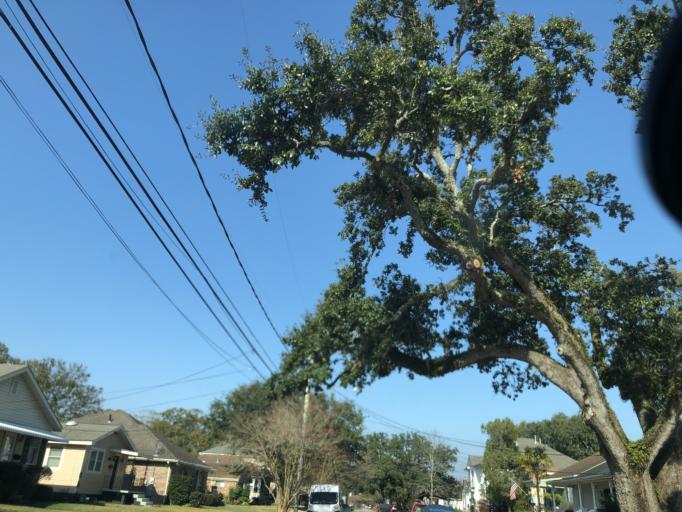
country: US
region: Louisiana
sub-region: Jefferson Parish
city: Metairie
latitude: 29.9829
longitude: -90.1528
